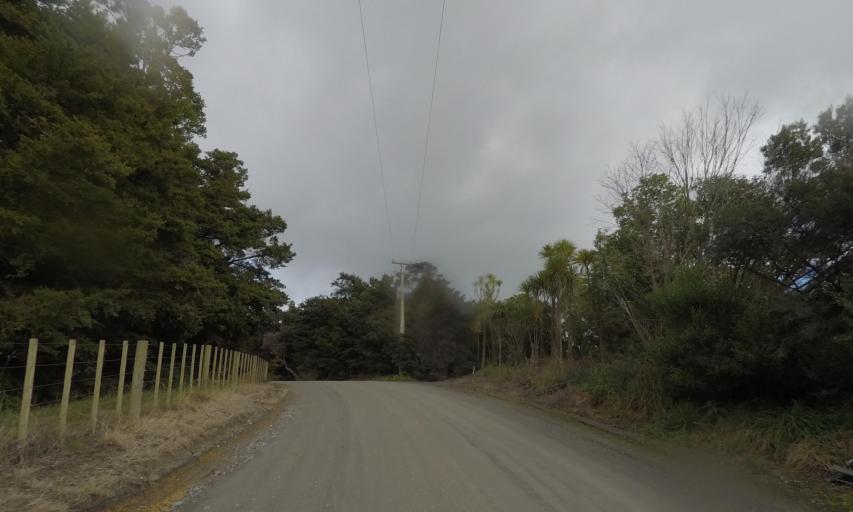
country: NZ
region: Auckland
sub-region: Auckland
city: Wellsford
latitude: -36.1691
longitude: 174.6019
